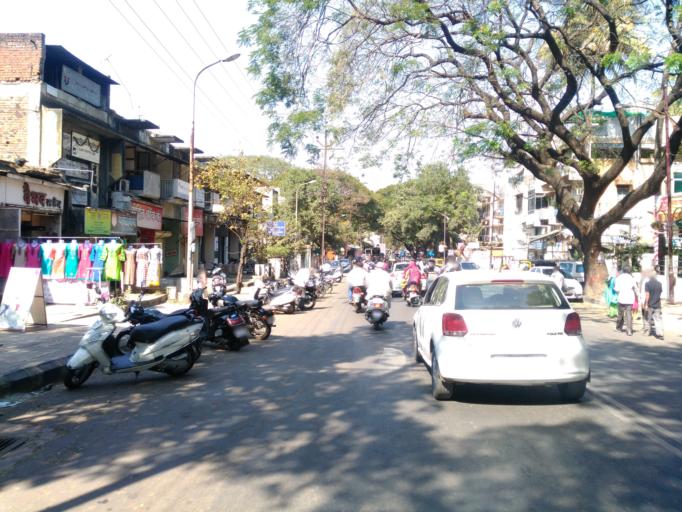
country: IN
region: Maharashtra
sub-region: Pune Division
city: Pune
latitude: 18.4882
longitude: 73.8499
